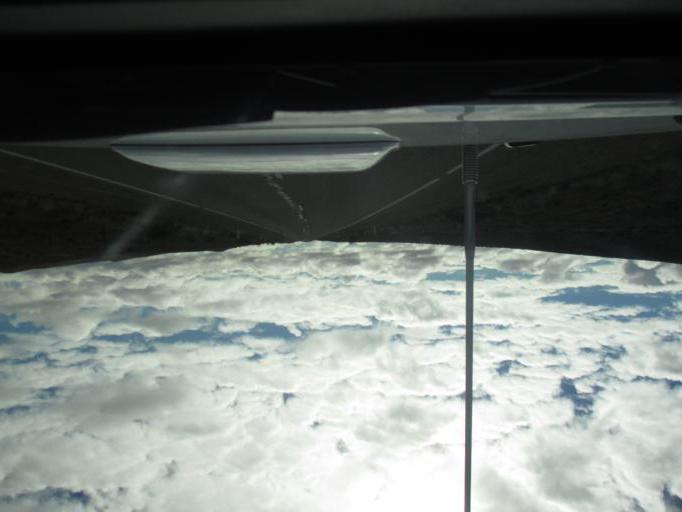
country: AU
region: South Australia
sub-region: Flinders Ranges
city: Quorn
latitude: -32.2592
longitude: 138.5064
